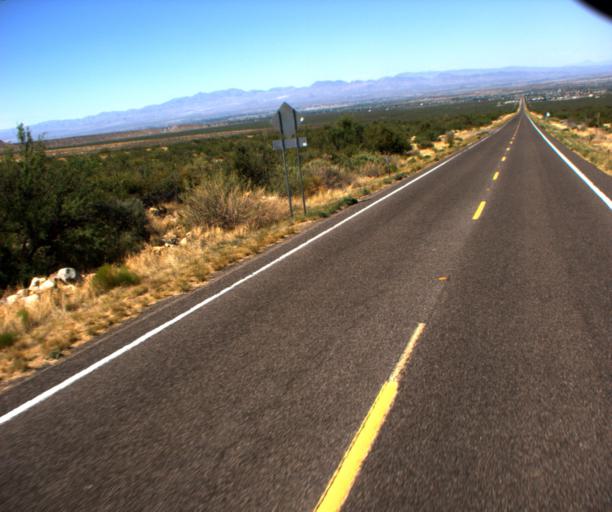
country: US
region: Arizona
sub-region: Graham County
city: Swift Trail Junction
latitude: 32.6921
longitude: -109.7521
